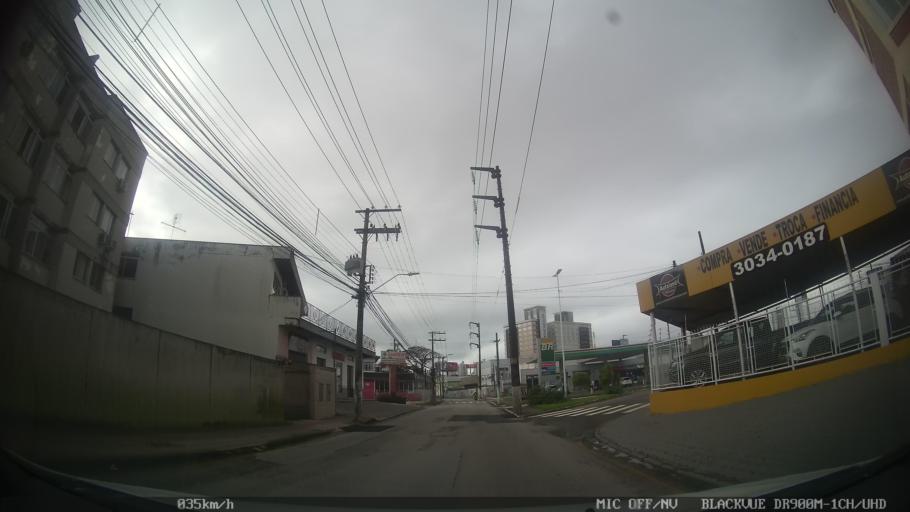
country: BR
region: Santa Catarina
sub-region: Sao Jose
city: Campinas
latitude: -27.5831
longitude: -48.6169
